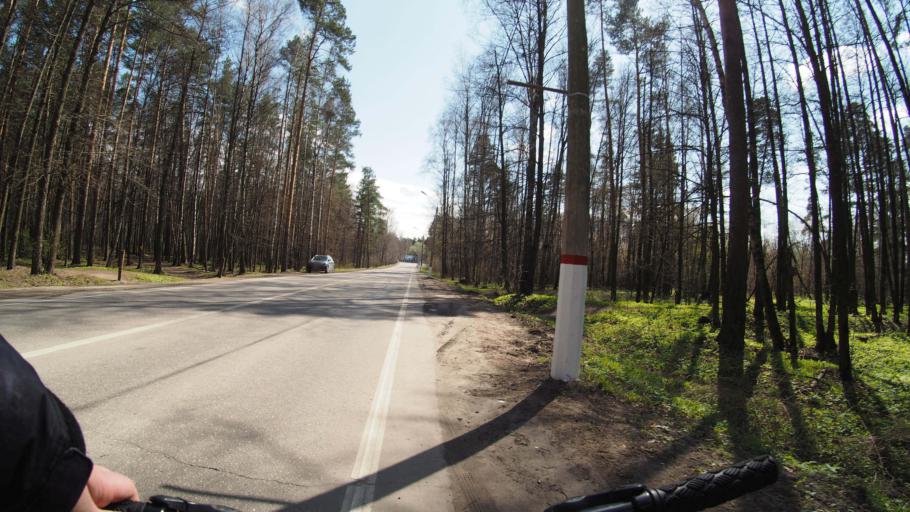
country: RU
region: Moskovskaya
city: Ramenskoye
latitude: 55.5811
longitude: 38.2282
